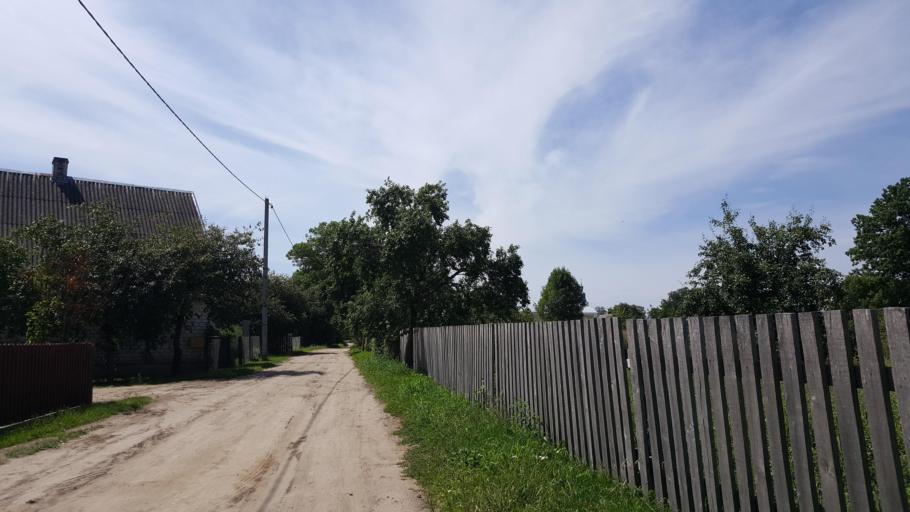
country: BY
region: Brest
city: Pruzhany
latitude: 52.5616
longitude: 24.2202
